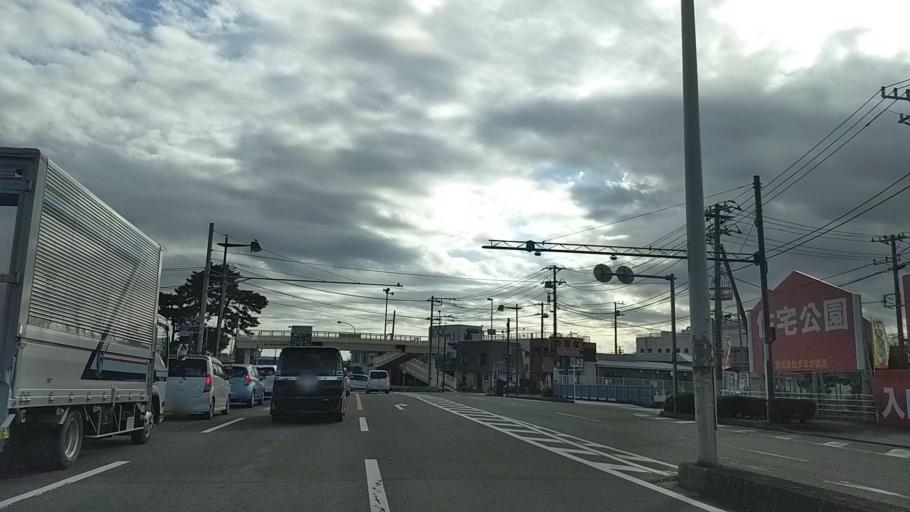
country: JP
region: Kanagawa
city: Odawara
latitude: 35.2789
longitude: 139.2047
